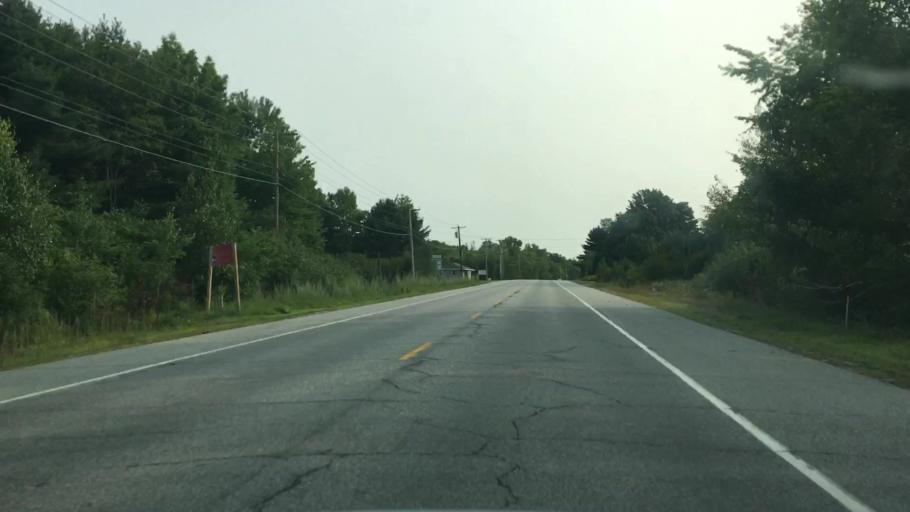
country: US
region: Maine
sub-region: Kennebec County
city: Gardiner
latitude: 44.2013
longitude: -69.7979
